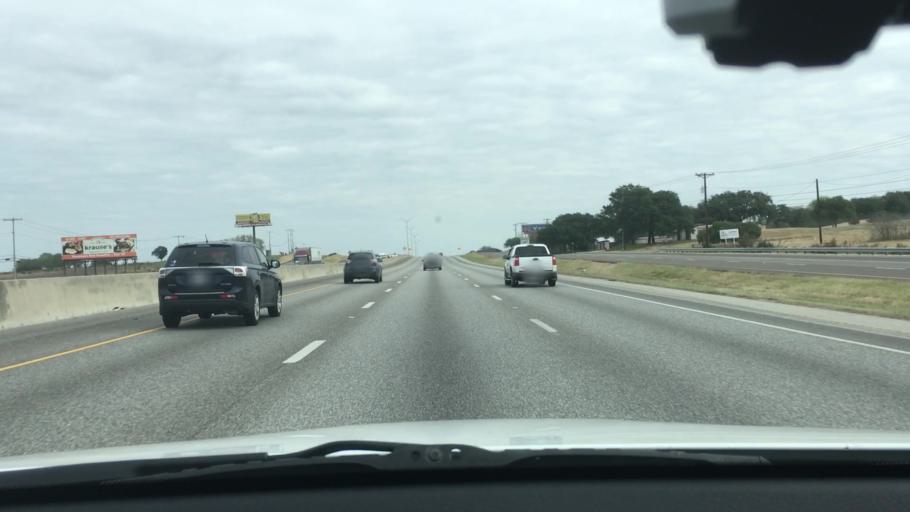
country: US
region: Texas
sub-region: Guadalupe County
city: Northcliff
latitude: 29.6299
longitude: -98.2323
